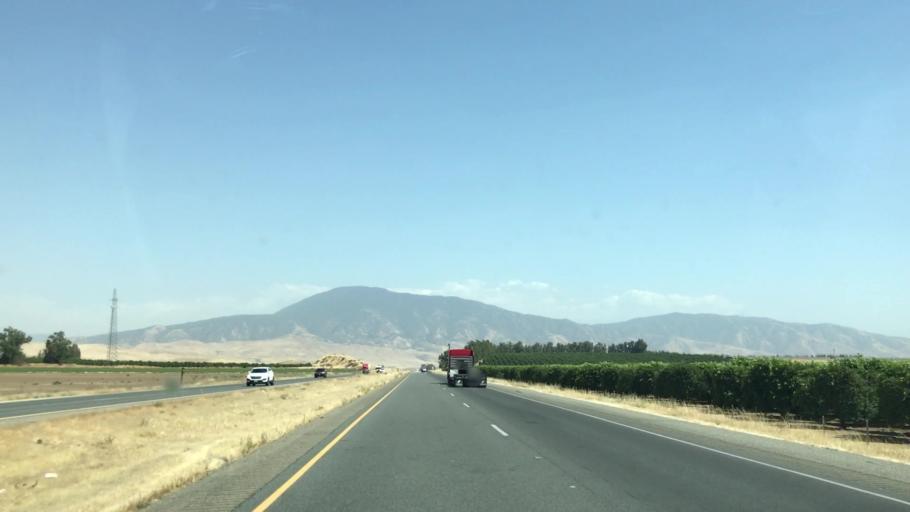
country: US
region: California
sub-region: Kern County
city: Arvin
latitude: 35.3232
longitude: -118.7963
